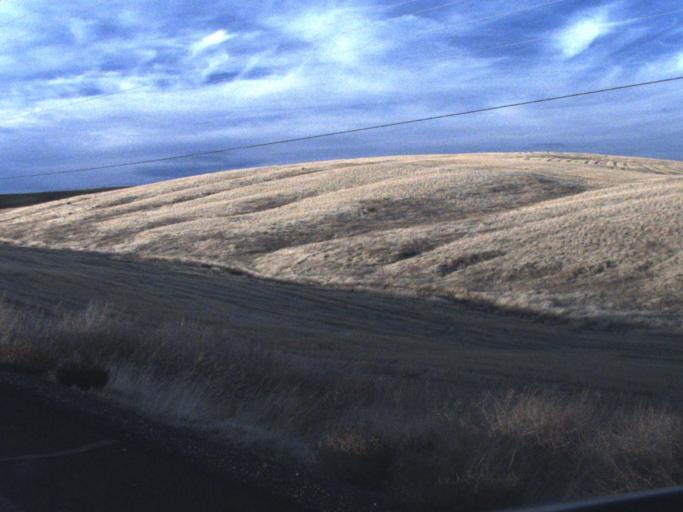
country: US
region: Washington
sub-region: Walla Walla County
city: Burbank
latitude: 46.0576
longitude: -118.7267
